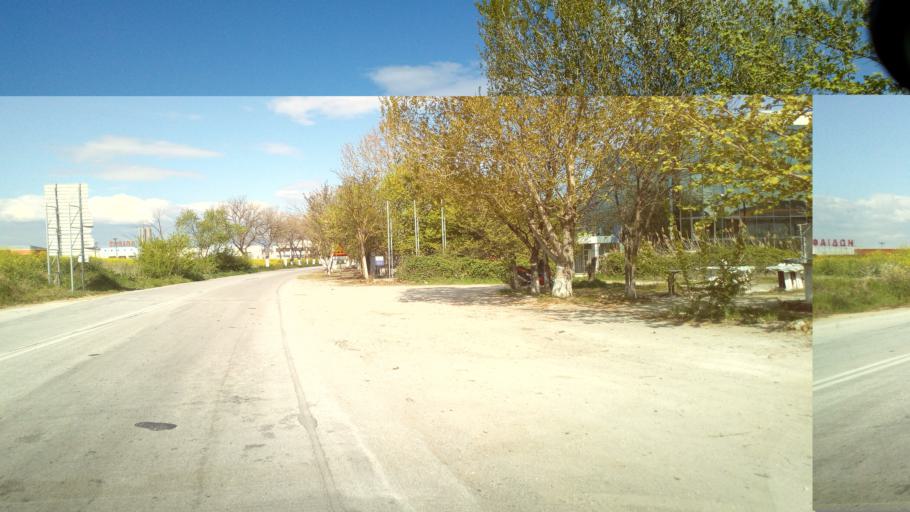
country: GR
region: Central Macedonia
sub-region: Nomos Kilkis
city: Nea Santa
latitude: 40.8422
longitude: 22.9057
